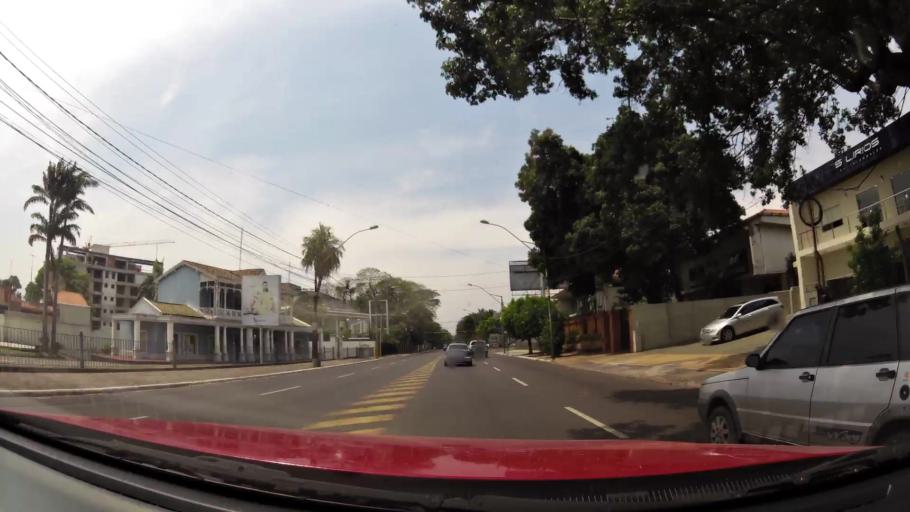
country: PY
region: Asuncion
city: Asuncion
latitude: -25.2932
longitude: -57.6072
